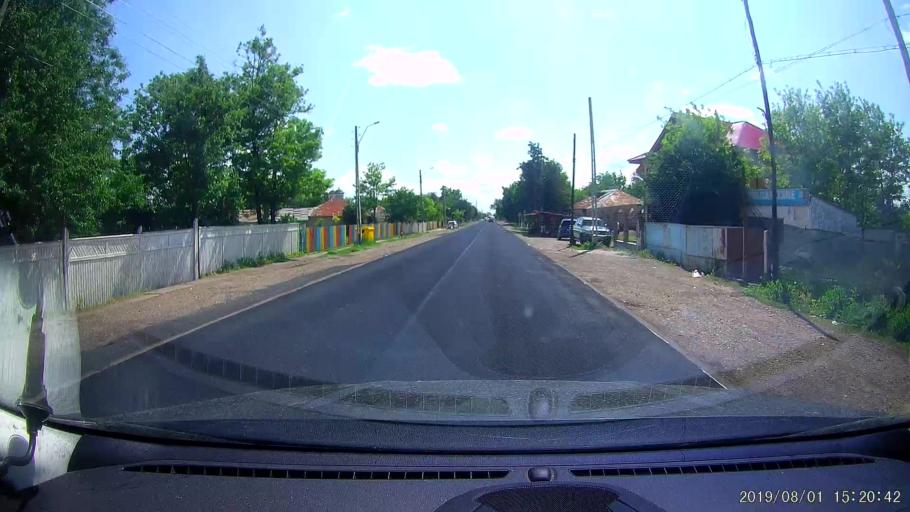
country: RO
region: Braila
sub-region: Comuna Tufesti
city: Tufesti
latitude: 45.0767
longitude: 27.8043
